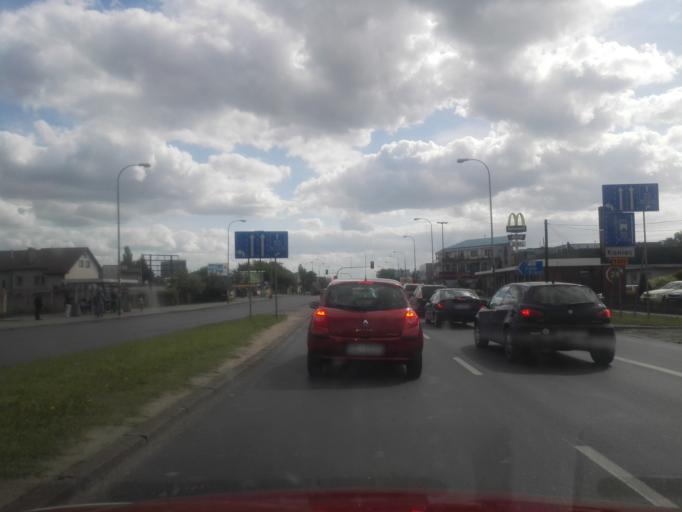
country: PL
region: Masovian Voivodeship
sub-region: Warszawa
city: Targowek
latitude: 52.2881
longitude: 21.0763
